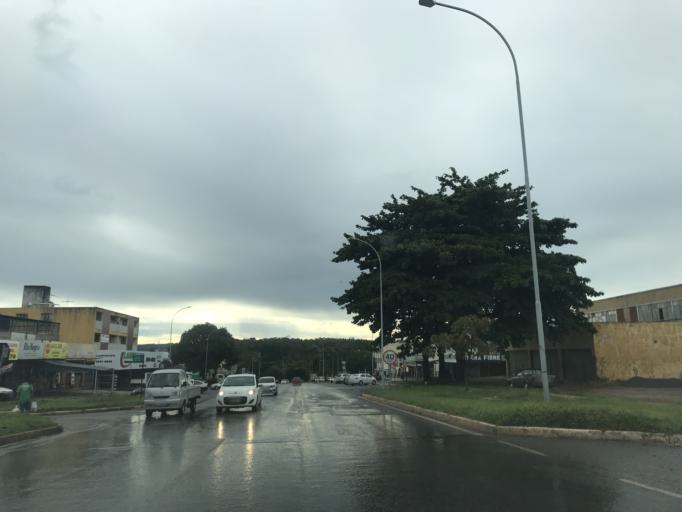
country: BR
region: Federal District
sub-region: Brasilia
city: Brasilia
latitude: -15.6423
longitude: -47.8065
